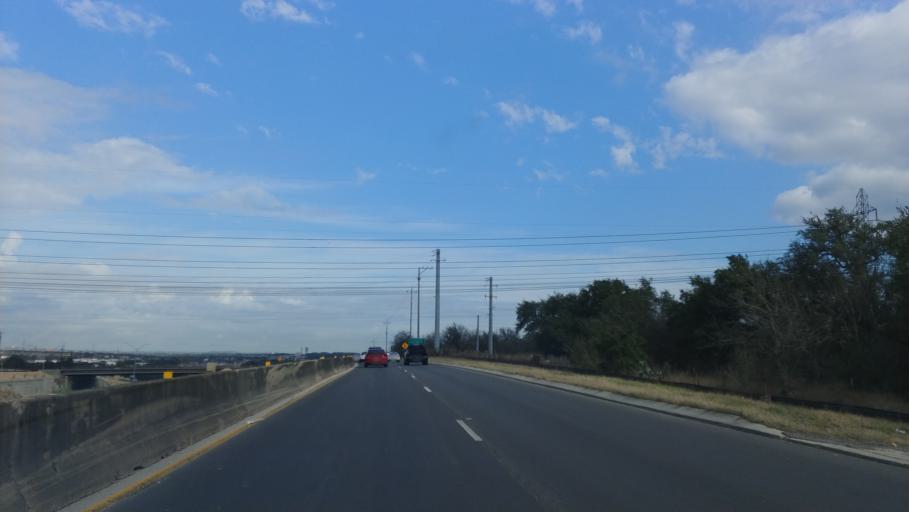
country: US
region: Texas
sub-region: Bexar County
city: Lackland Air Force Base
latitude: 29.4140
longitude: -98.7092
